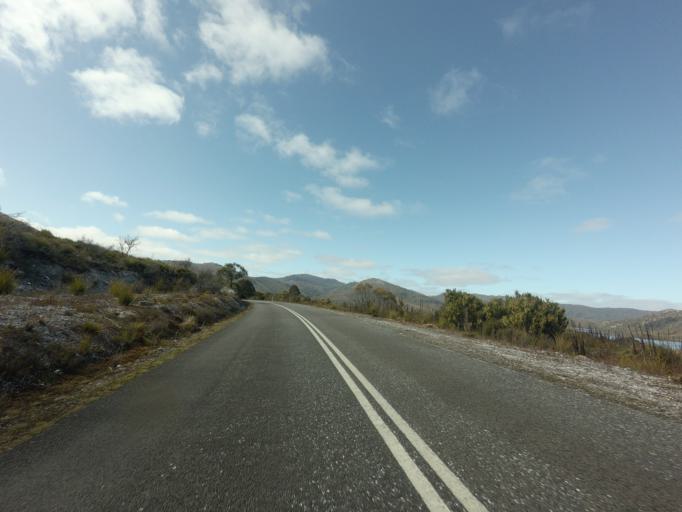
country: AU
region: Tasmania
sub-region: Huon Valley
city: Geeveston
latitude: -42.8389
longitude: 146.1582
